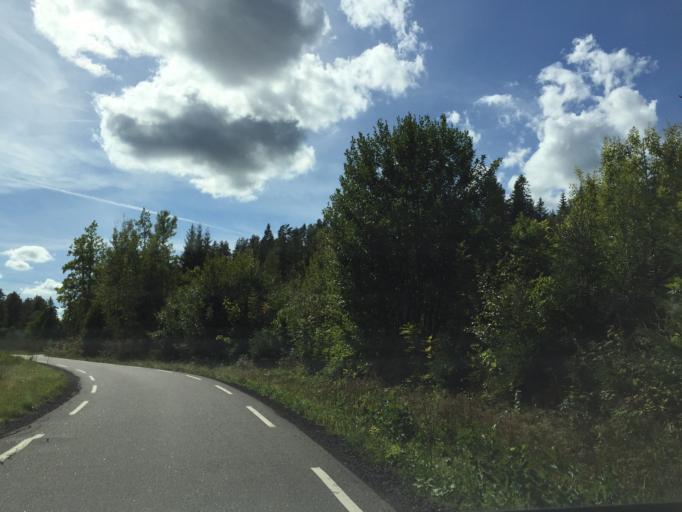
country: NO
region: Vestfold
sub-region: Holmestrand
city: Gullhaug
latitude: 59.4360
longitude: 10.1600
